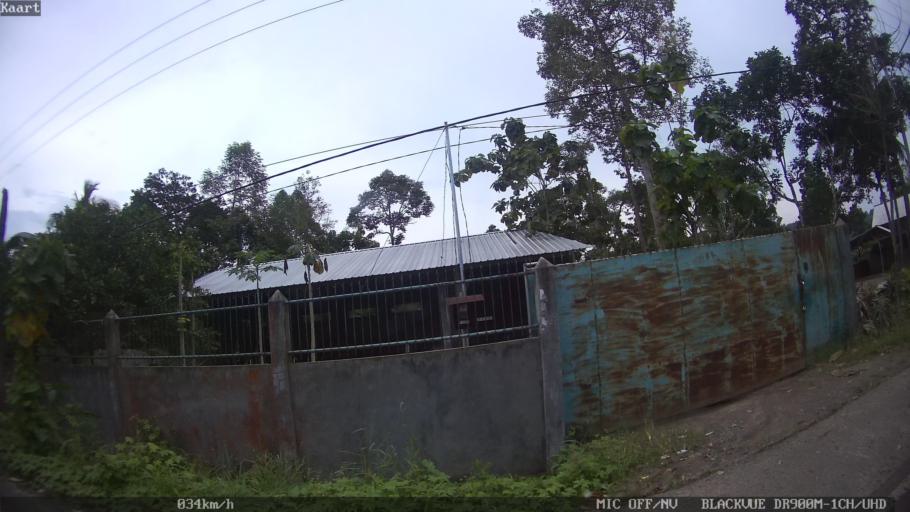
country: ID
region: Lampung
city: Bandarlampung
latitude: -5.4363
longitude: 105.2219
